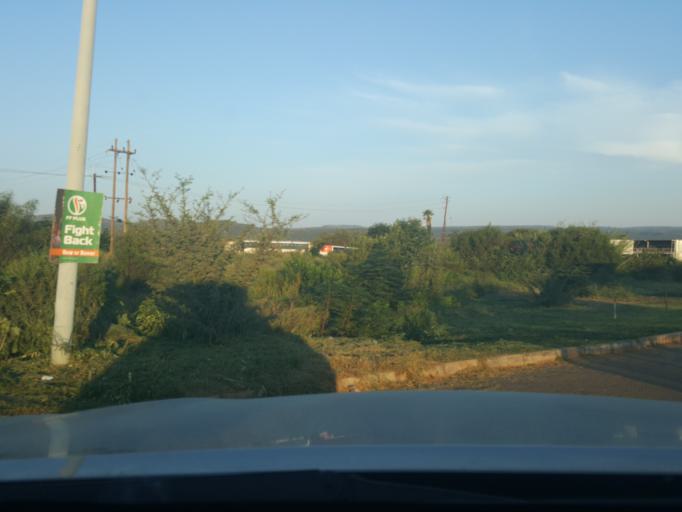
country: ZA
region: North-West
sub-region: Ngaka Modiri Molema District Municipality
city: Zeerust
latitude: -25.5426
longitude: 26.0859
